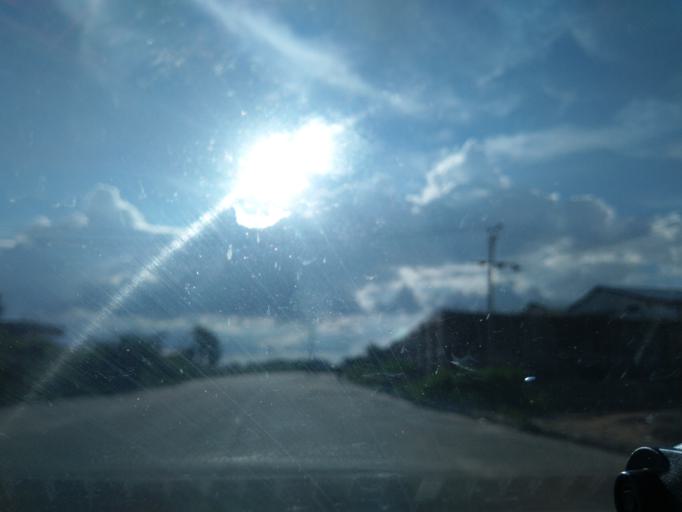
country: NG
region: Abuja Federal Capital Territory
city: Abuja
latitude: 9.0298
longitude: 7.4008
